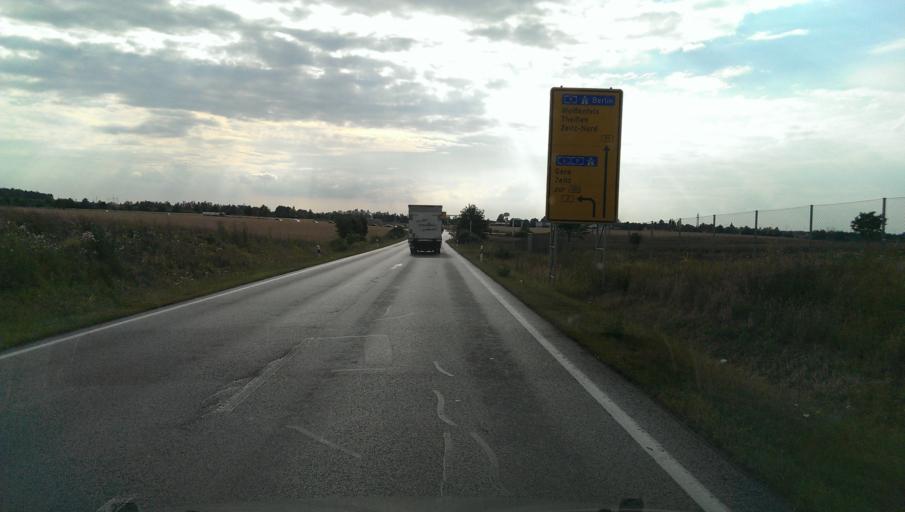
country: DE
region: Saxony-Anhalt
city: Theissen
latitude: 51.0790
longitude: 12.1232
